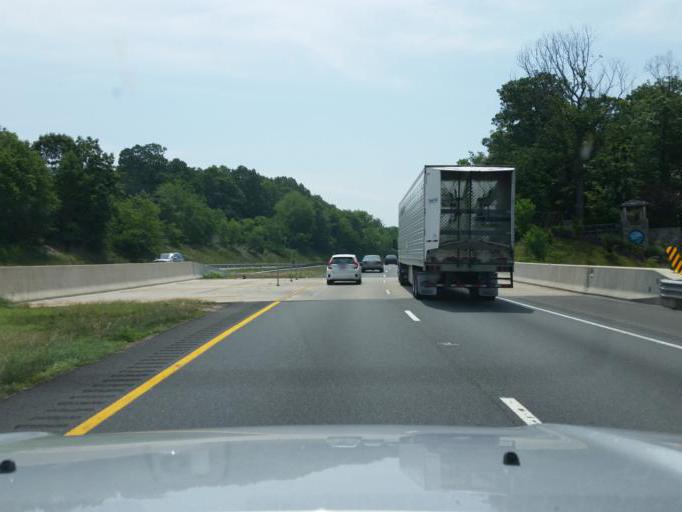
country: US
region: Maryland
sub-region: Frederick County
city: Urbana
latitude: 39.2960
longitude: -77.3343
